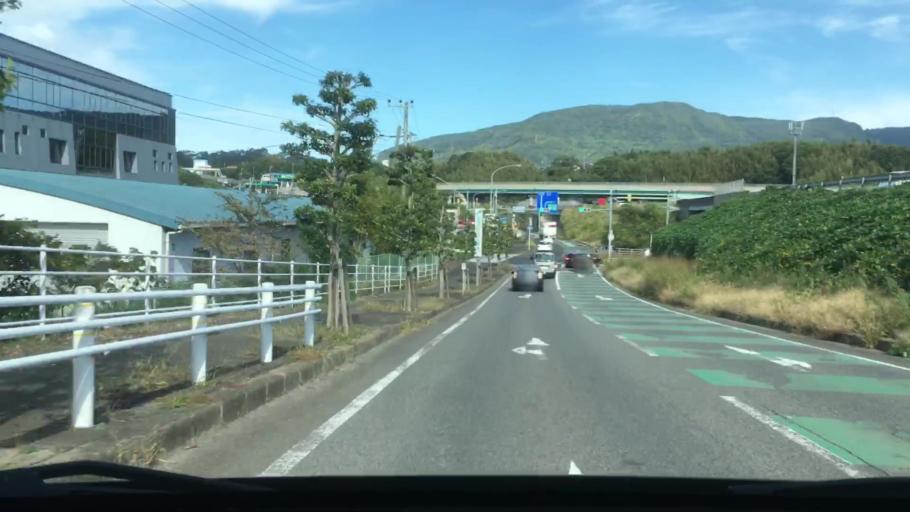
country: JP
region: Nagasaki
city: Sasebo
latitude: 33.1444
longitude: 129.7791
